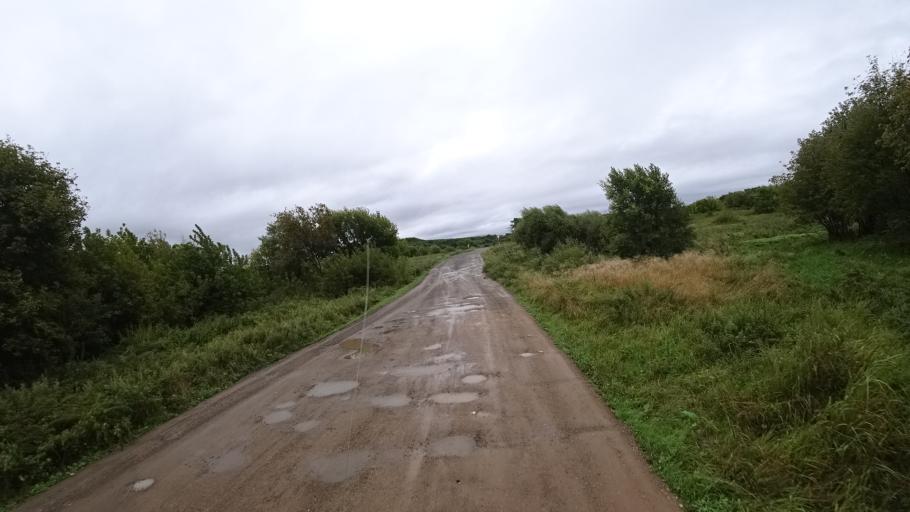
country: RU
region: Primorskiy
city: Monastyrishche
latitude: 44.2769
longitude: 132.4228
